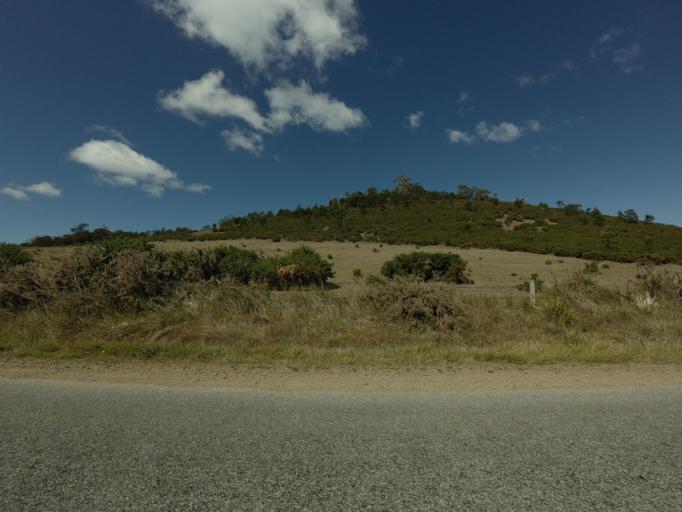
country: AU
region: Tasmania
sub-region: Break O'Day
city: St Helens
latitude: -41.9566
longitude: 148.1651
